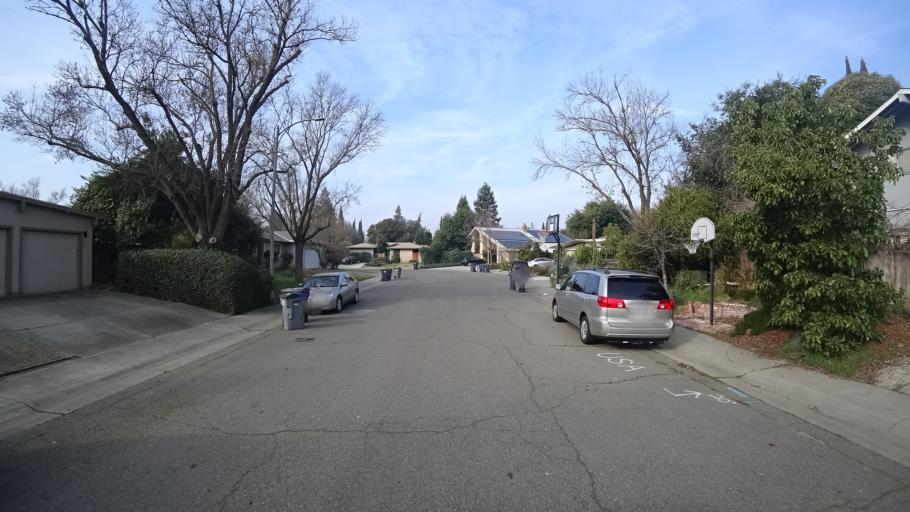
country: US
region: California
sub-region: Yolo County
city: Davis
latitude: 38.5578
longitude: -121.7632
